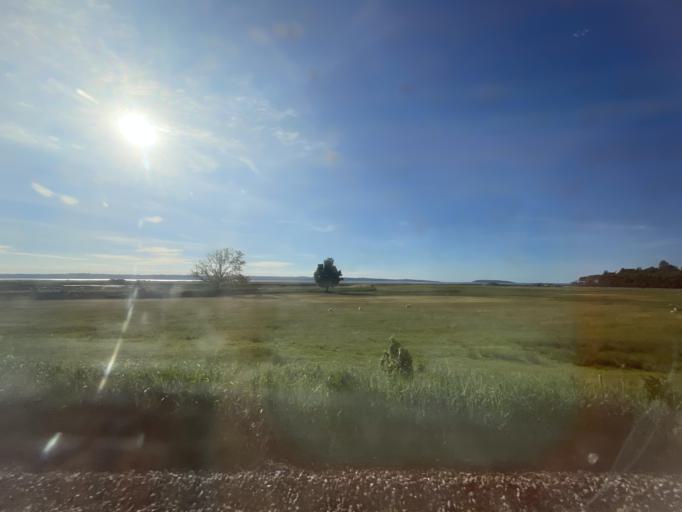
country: GB
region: Wales
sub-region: Conwy
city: Llanfairfechan
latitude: 53.2511
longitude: -3.9936
